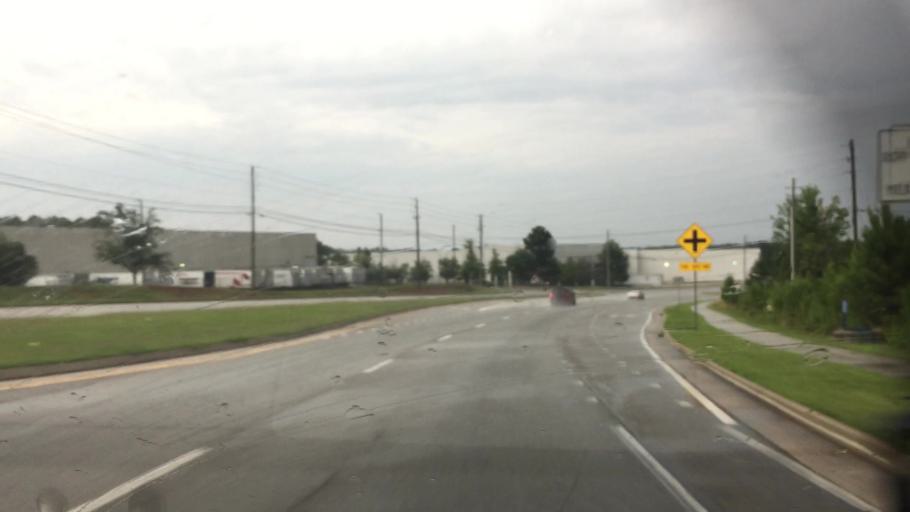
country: US
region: Georgia
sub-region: Henry County
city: Stockbridge
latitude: 33.5176
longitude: -84.2049
